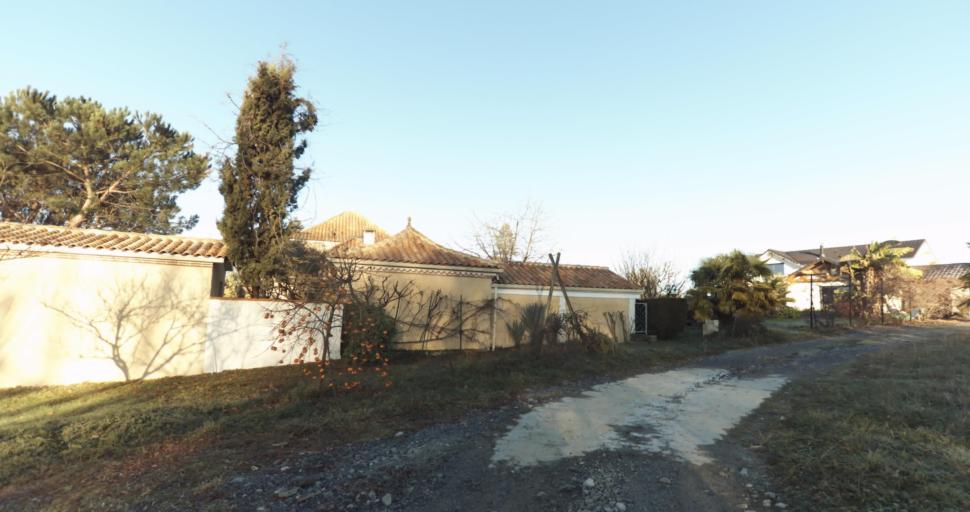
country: FR
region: Aquitaine
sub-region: Departement des Pyrenees-Atlantiques
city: Morlaas
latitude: 43.3314
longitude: -0.2696
